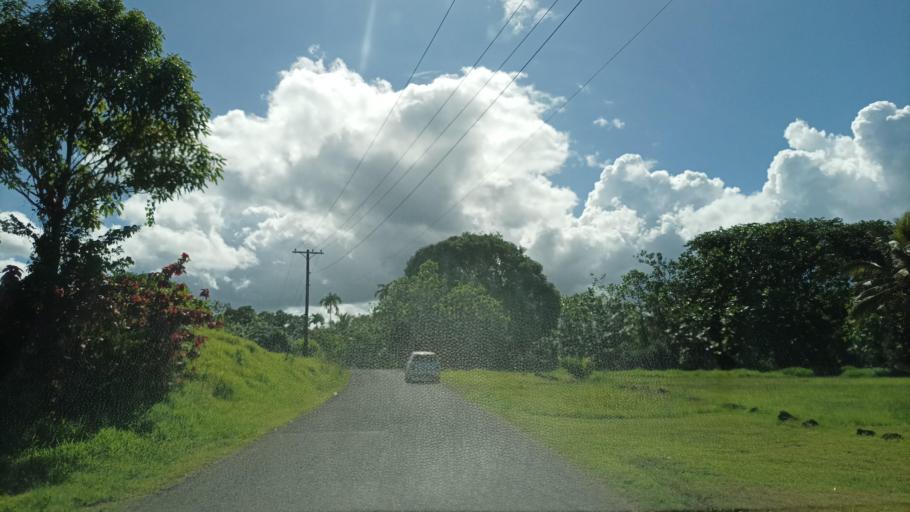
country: FM
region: Pohnpei
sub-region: Madolenihm Municipality
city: Madolenihm Municipality Government
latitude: 6.8427
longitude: 158.3079
